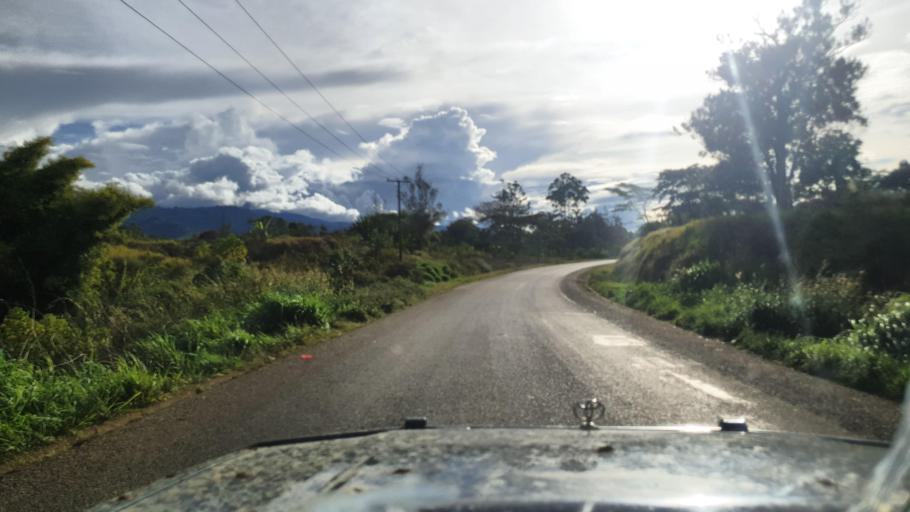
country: PG
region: Jiwaka
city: Minj
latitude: -5.8825
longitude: 144.6849
